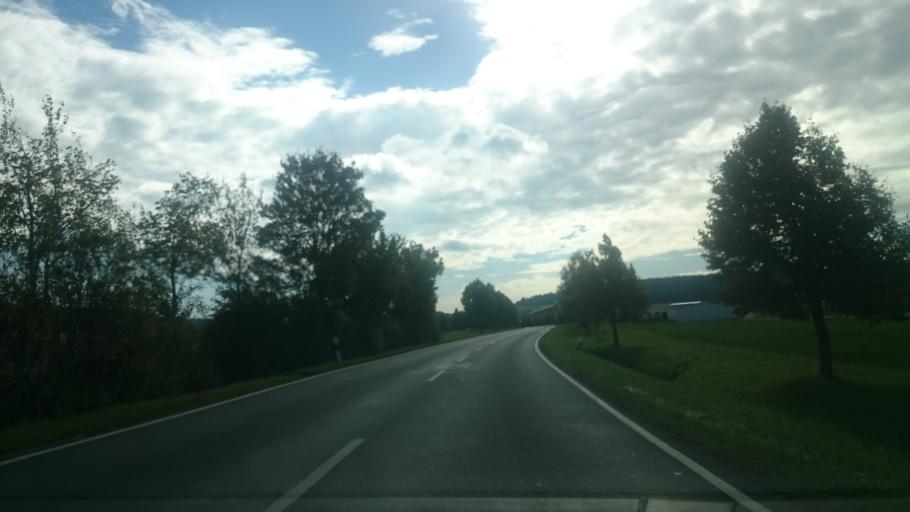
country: DE
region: Bavaria
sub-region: Regierungsbezirk Mittelfranken
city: Thalmassing
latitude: 49.1505
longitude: 11.2591
